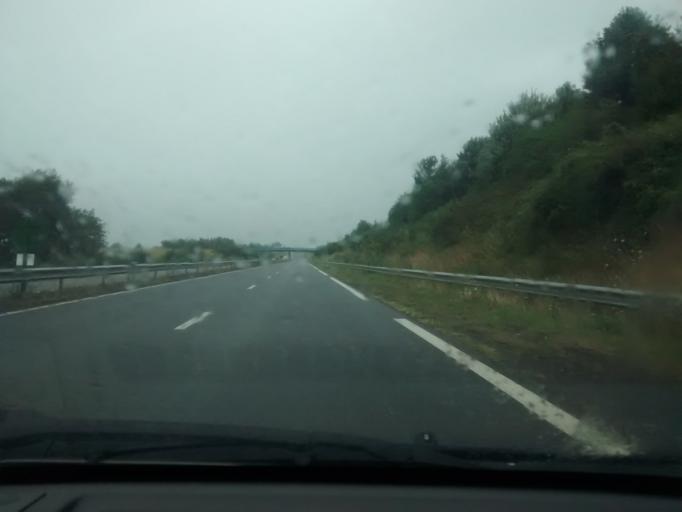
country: FR
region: Brittany
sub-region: Departement d'Ille-et-Vilaine
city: Betton
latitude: 48.1579
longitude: -1.6253
